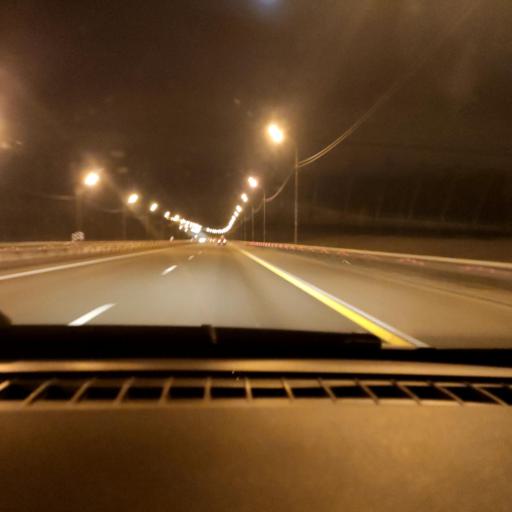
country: RU
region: Lipetsk
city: Khlevnoye
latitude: 52.2287
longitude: 39.0956
